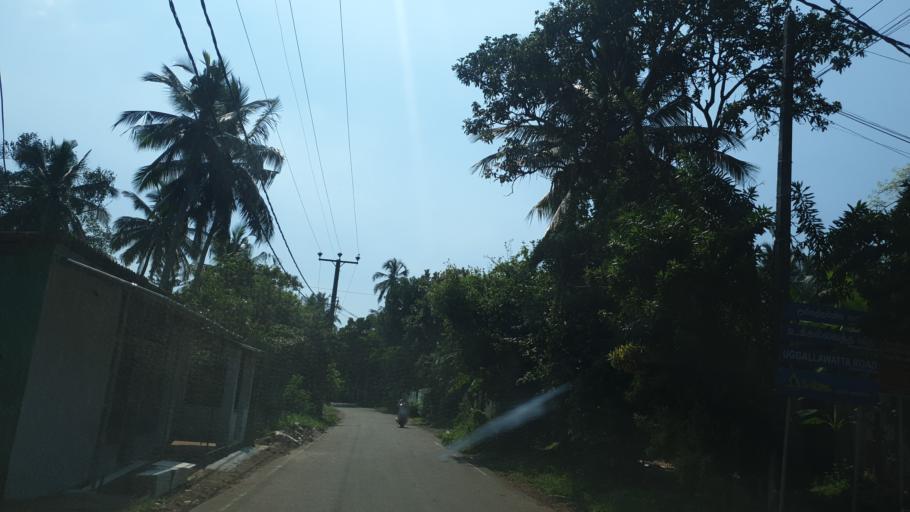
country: LK
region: Western
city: Moratuwa
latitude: 6.7628
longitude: 79.9288
